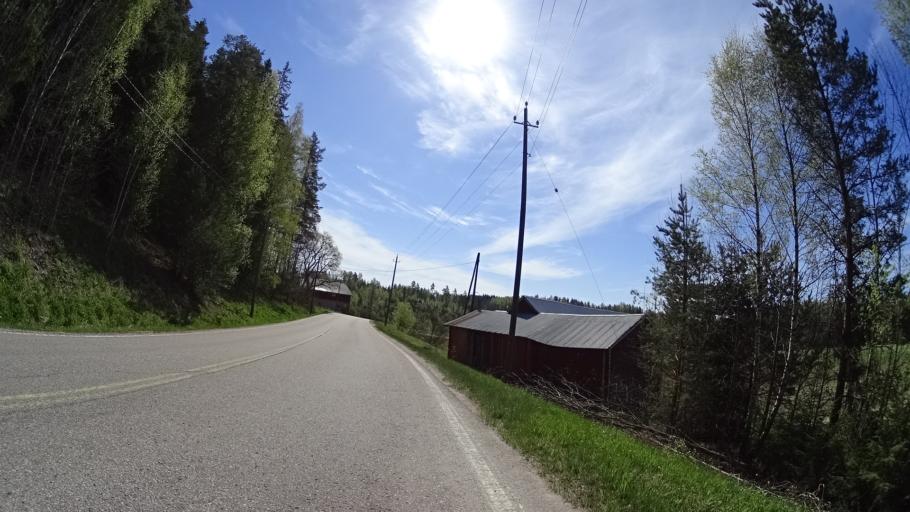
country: FI
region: Uusimaa
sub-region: Helsinki
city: Nurmijaervi
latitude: 60.3816
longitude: 24.8366
